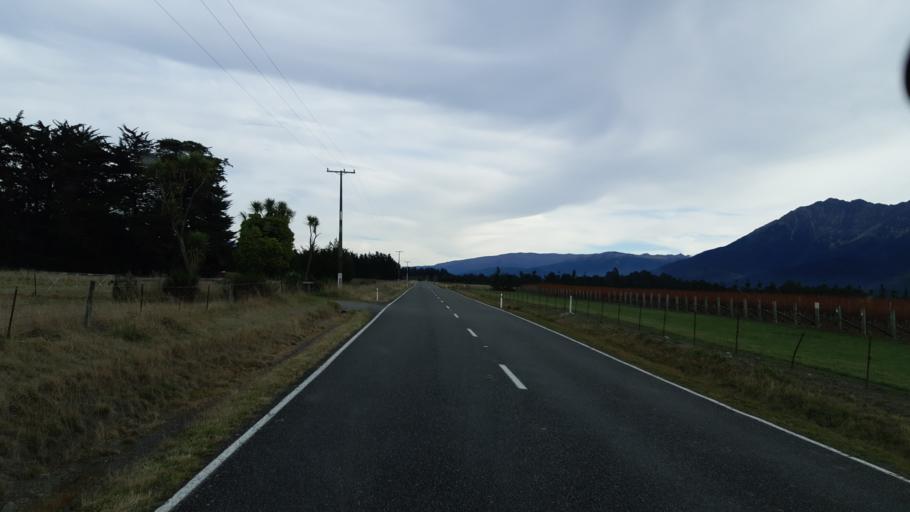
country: NZ
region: Tasman
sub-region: Tasman District
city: Brightwater
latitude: -41.6254
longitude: 173.3476
